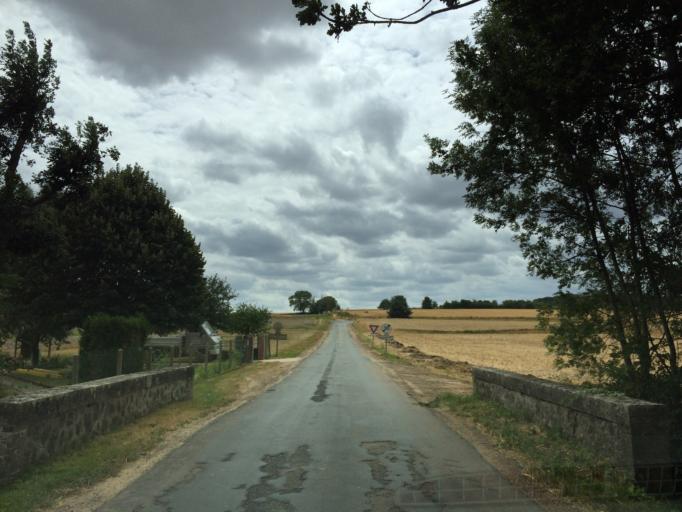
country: FR
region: Bourgogne
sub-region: Departement de l'Yonne
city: Fleury-la-Vallee
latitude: 47.8412
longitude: 3.4020
